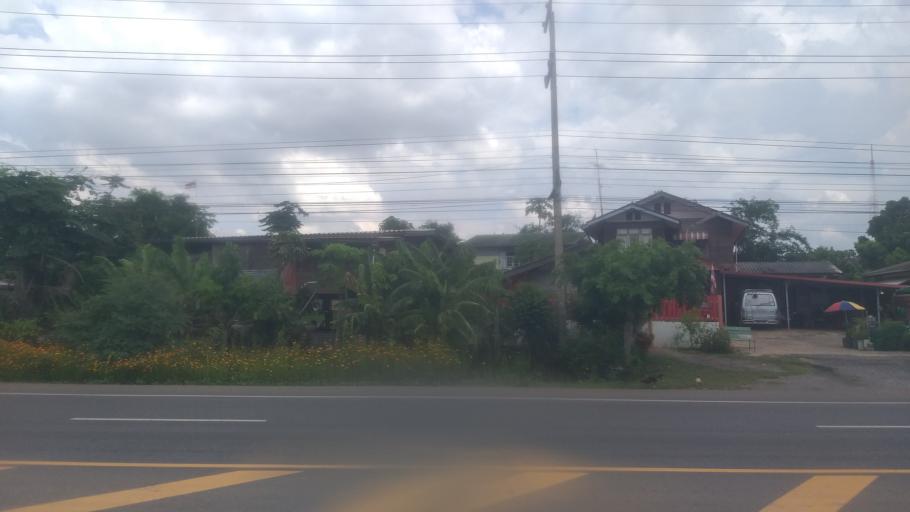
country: TH
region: Chaiyaphum
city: Noen Sa-nga
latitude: 15.6727
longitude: 101.9635
